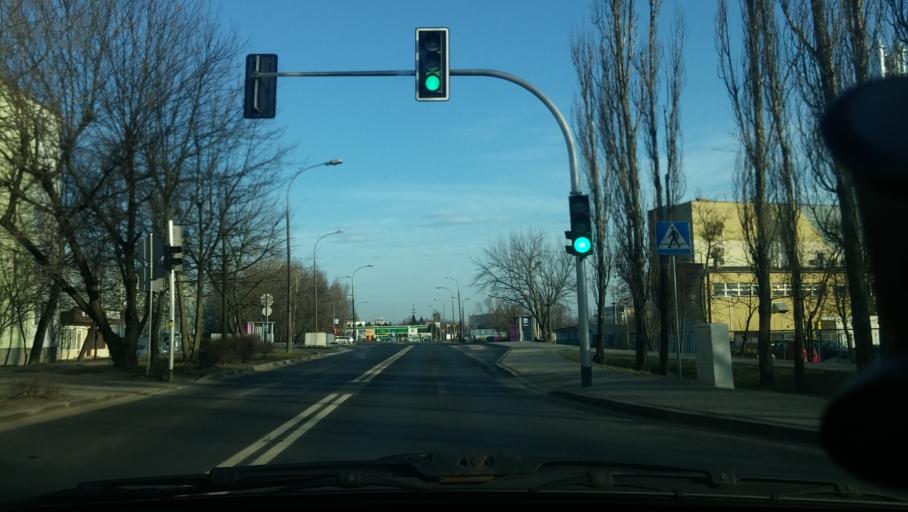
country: PL
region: Masovian Voivodeship
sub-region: Powiat piaseczynski
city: Piaseczno
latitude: 52.0791
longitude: 21.0217
